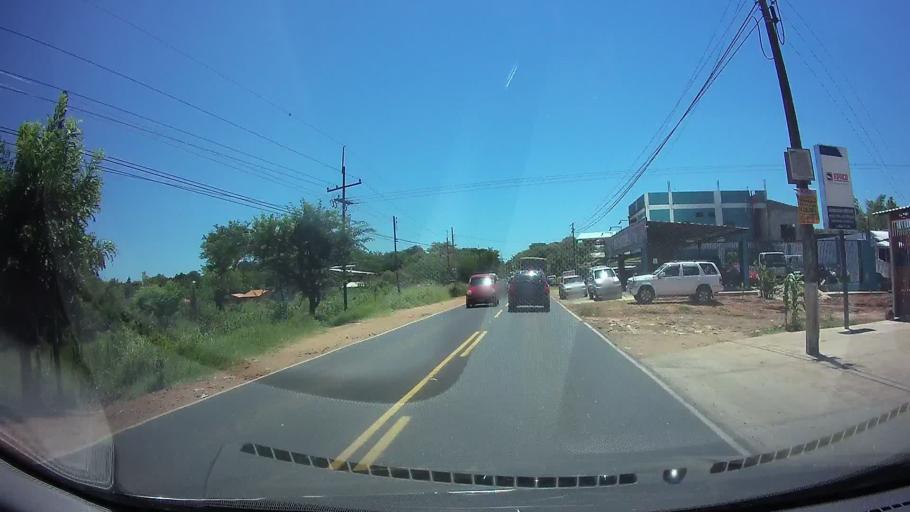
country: PY
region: Central
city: Limpio
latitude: -25.2494
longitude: -57.4879
